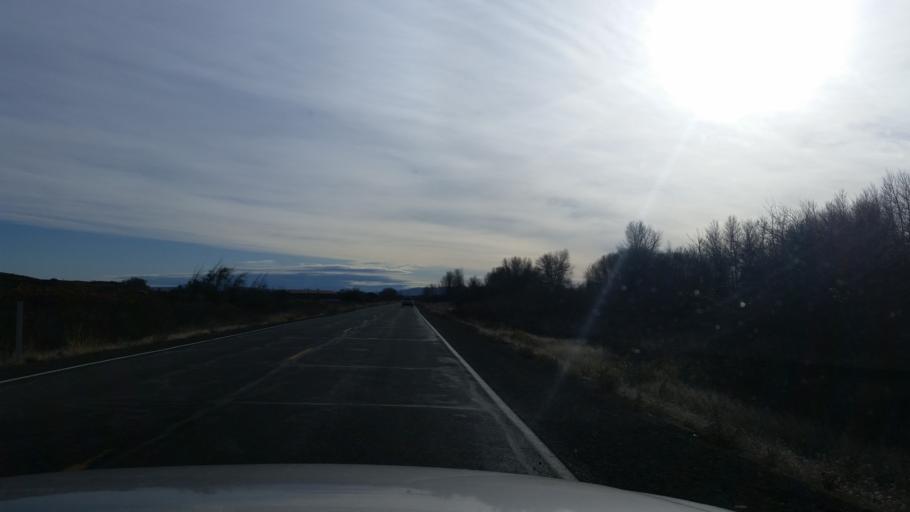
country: US
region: Washington
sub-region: Kittitas County
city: Ellensburg
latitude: 47.0484
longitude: -120.6311
